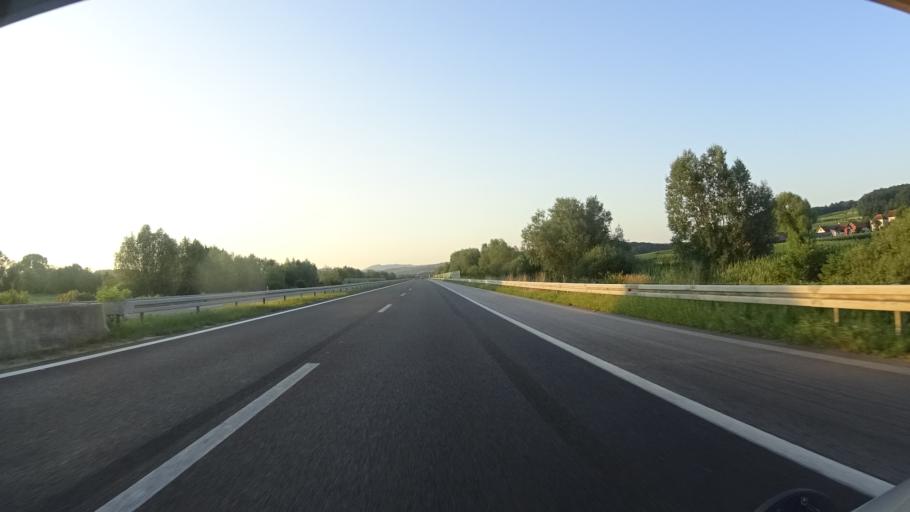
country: HR
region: Varazdinska
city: Remetinec
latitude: 46.0431
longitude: 16.2964
